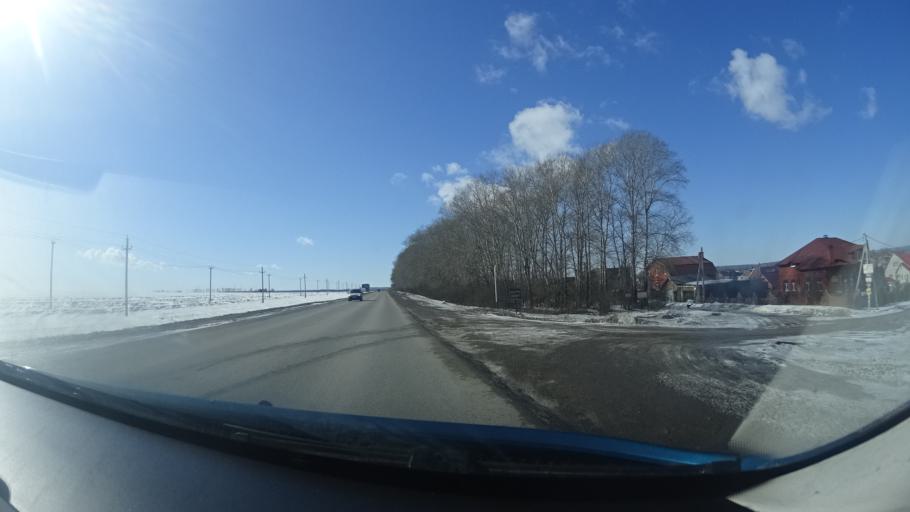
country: RU
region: Bashkortostan
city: Avdon
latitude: 54.6067
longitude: 55.8582
